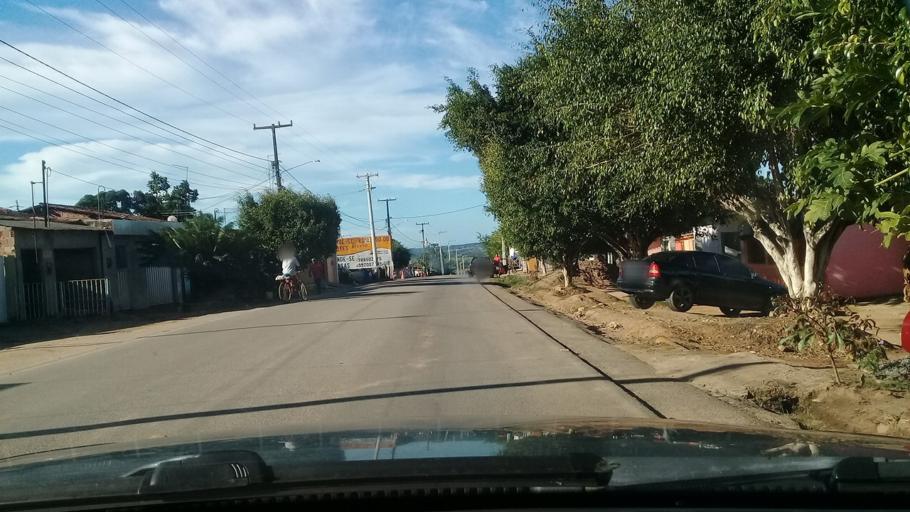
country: BR
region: Pernambuco
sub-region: Gloria Do Goita
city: Gloria do Goita
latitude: -7.9924
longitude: -35.2068
